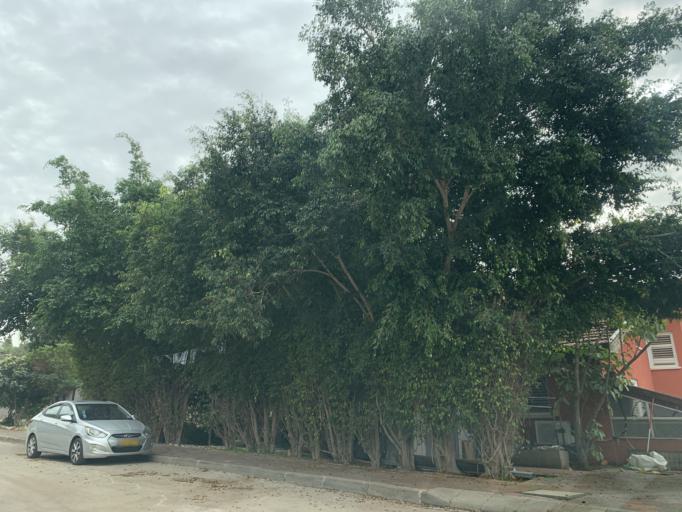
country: IL
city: Nirit
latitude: 32.1469
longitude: 34.9827
